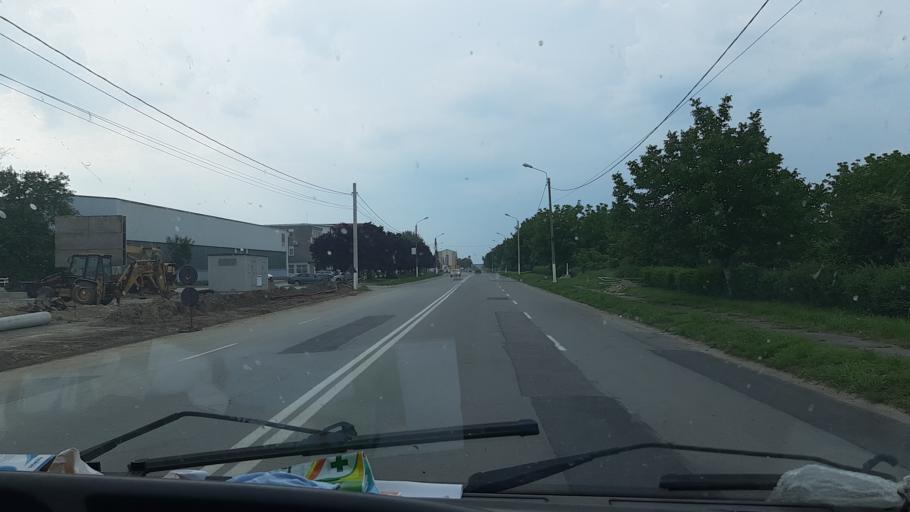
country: RO
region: Timis
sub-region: Municipiul Lugoj
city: Lugoj
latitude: 45.7042
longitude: 21.8909
